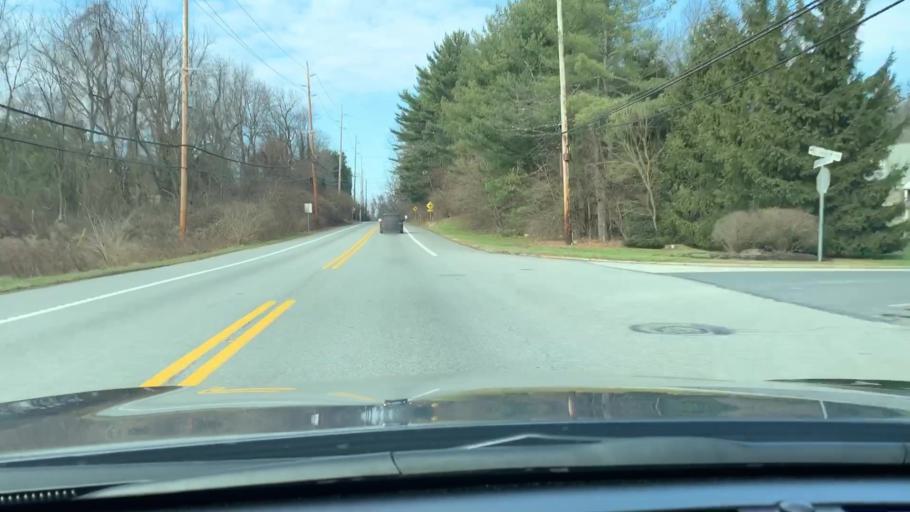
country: US
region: Pennsylvania
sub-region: Chester County
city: Berwyn
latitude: 40.0130
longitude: -75.4313
